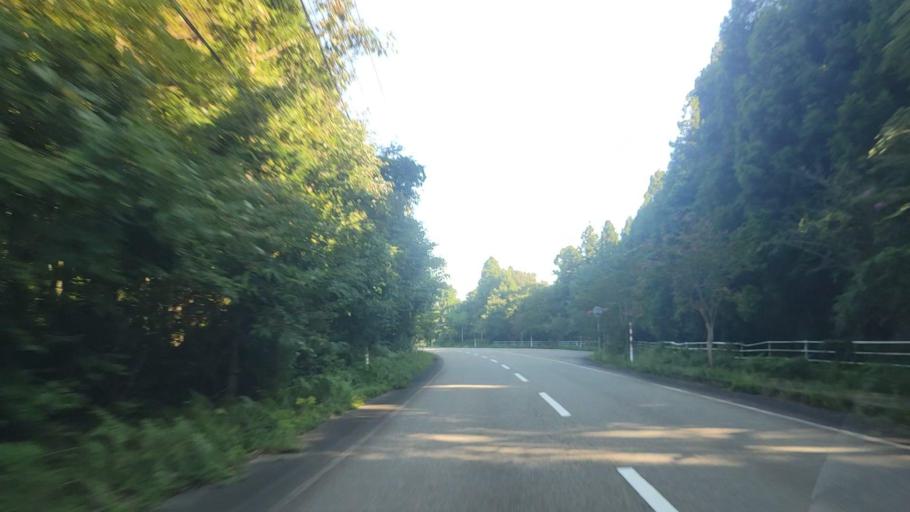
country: JP
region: Ishikawa
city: Nanao
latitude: 37.1260
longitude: 136.9256
